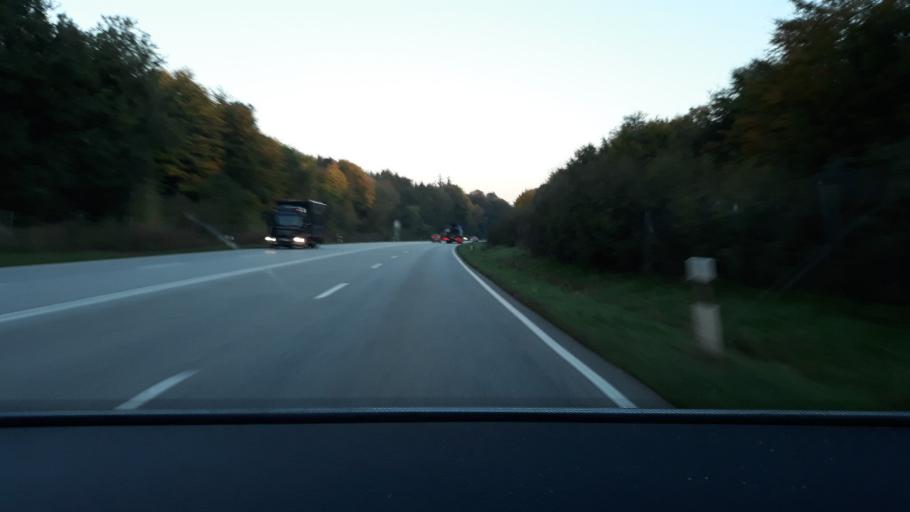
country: DE
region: Schleswig-Holstein
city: Schuby
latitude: 54.5160
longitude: 9.5135
